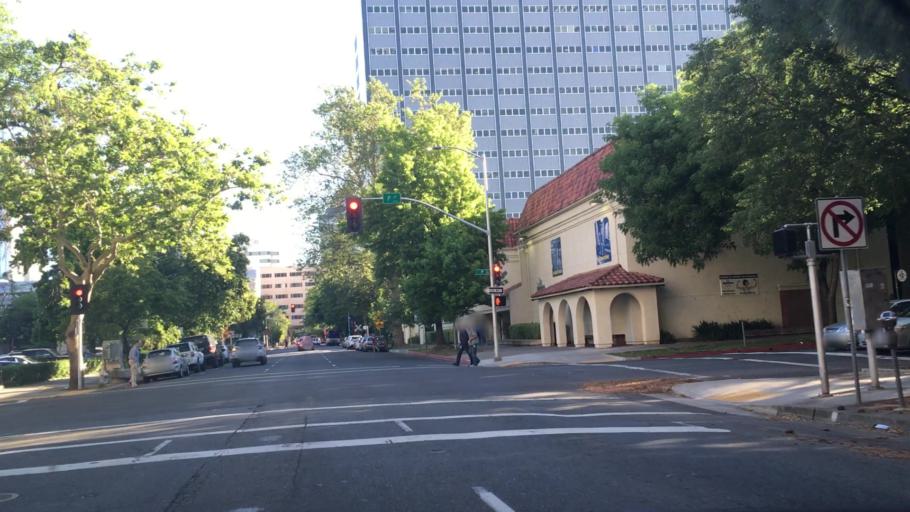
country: US
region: California
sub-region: Sacramento County
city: Sacramento
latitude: 38.5742
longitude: -121.4991
